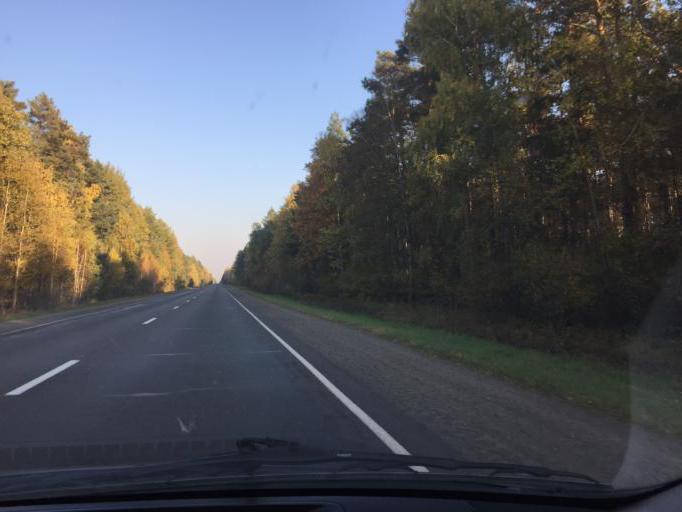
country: BY
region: Brest
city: Mikashevichy
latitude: 52.2387
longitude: 27.2851
